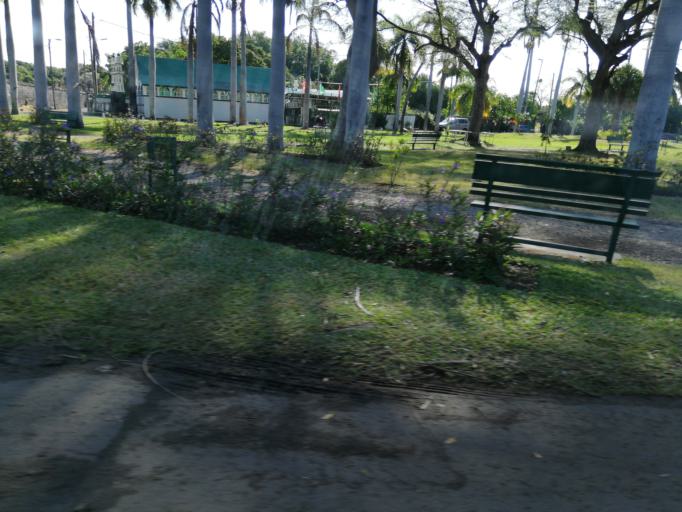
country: MU
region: Port Louis
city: Port Louis
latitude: -20.1579
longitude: 57.4871
